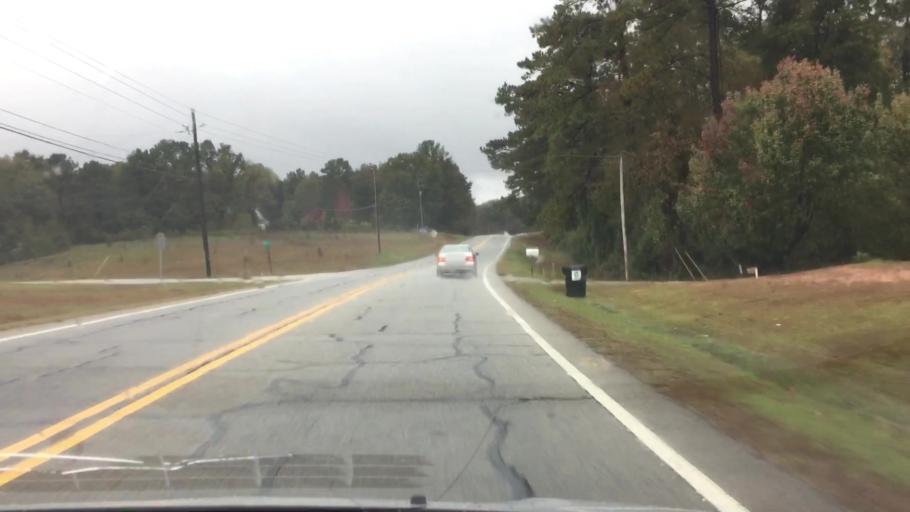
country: US
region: Georgia
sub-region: Henry County
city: Stockbridge
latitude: 33.5720
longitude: -84.1472
